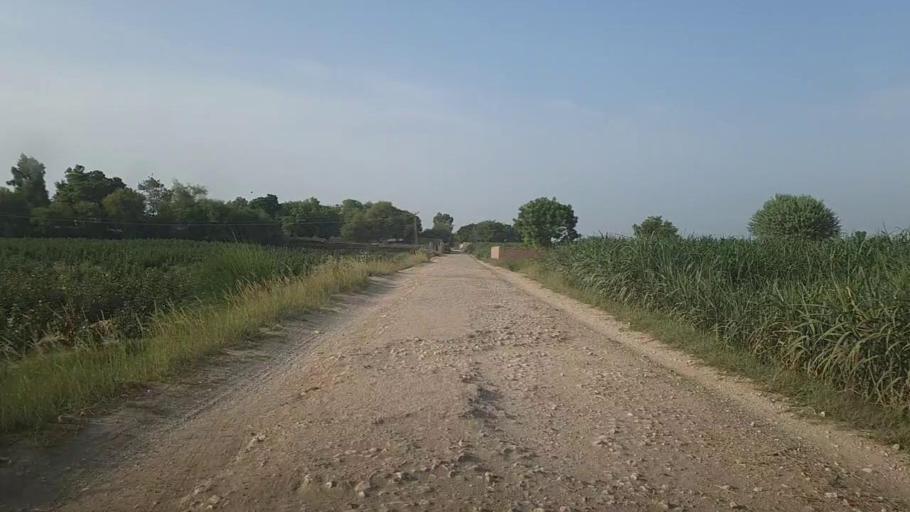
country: PK
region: Sindh
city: Ubauro
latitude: 28.3240
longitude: 69.7961
